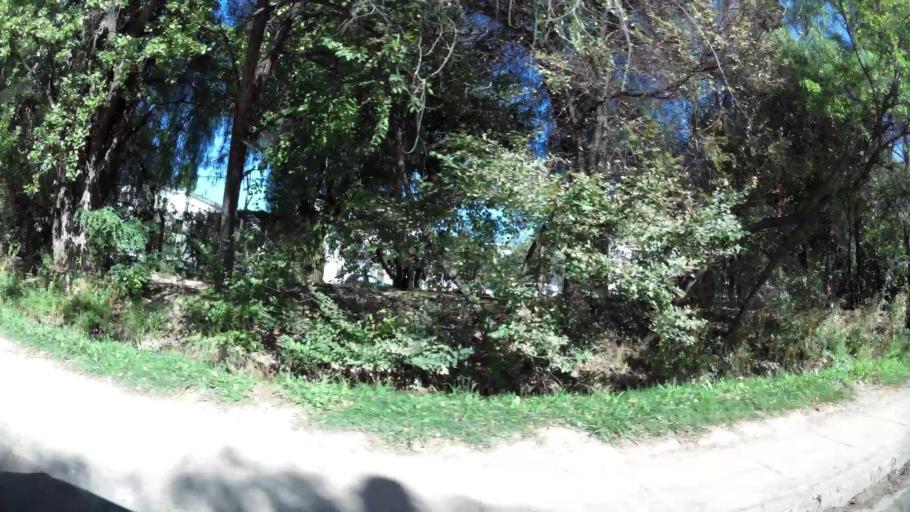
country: AR
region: Mendoza
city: Mendoza
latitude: -32.8831
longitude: -68.8736
